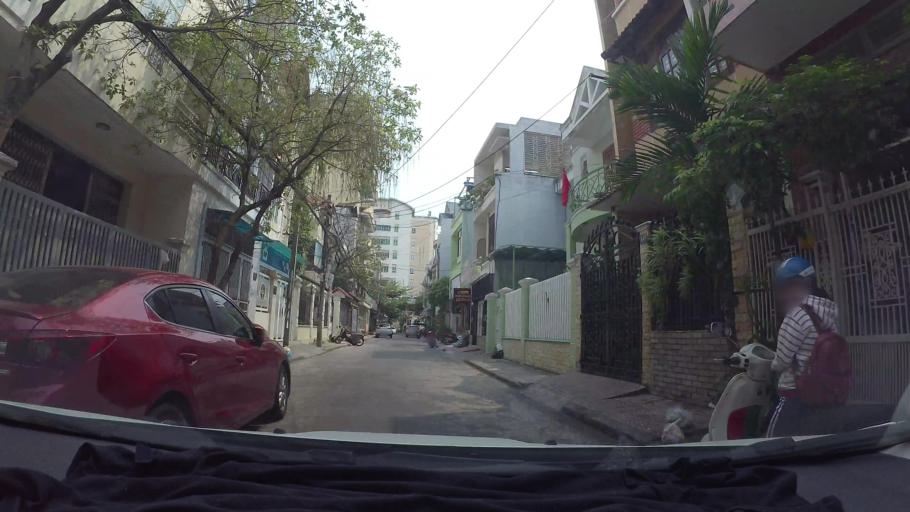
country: VN
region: Da Nang
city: Son Tra
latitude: 16.0433
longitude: 108.2225
